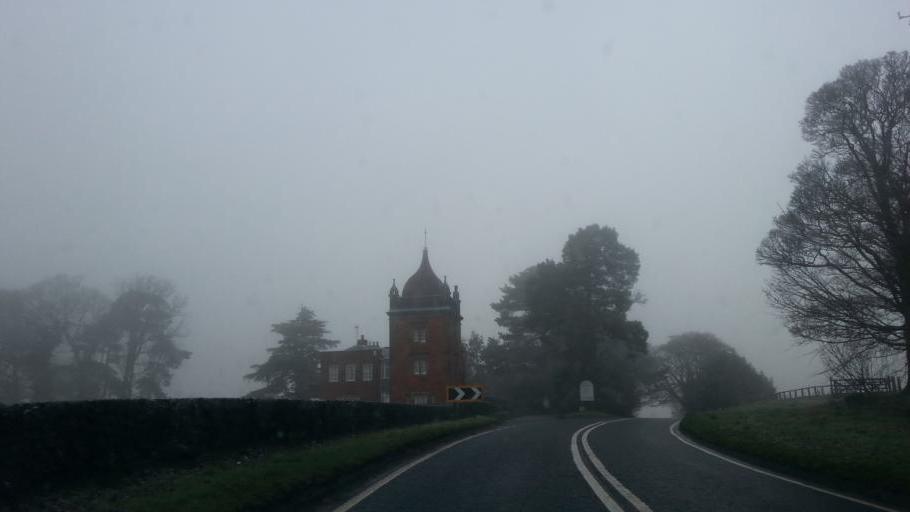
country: GB
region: England
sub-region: Cheshire East
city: Siddington
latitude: 53.2571
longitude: -2.2350
